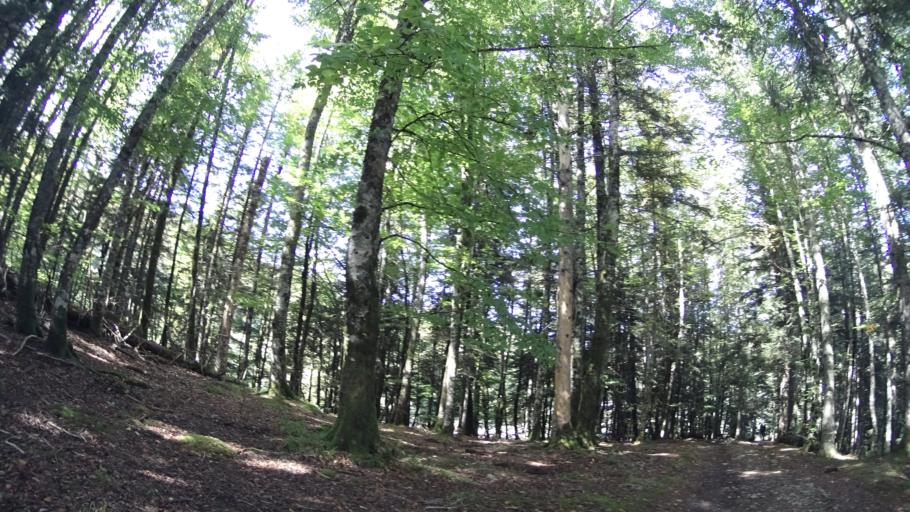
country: ES
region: Navarre
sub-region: Provincia de Navarra
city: Orbara
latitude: 42.9872
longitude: -1.1386
